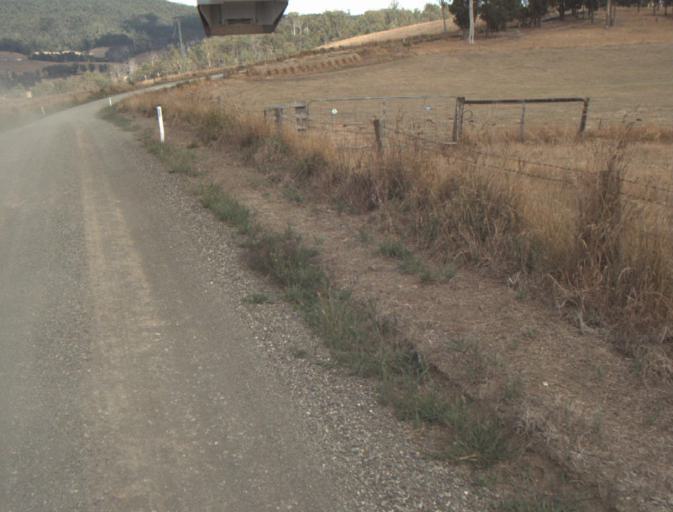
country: AU
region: Tasmania
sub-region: Launceston
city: Mayfield
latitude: -41.2196
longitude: 147.1446
